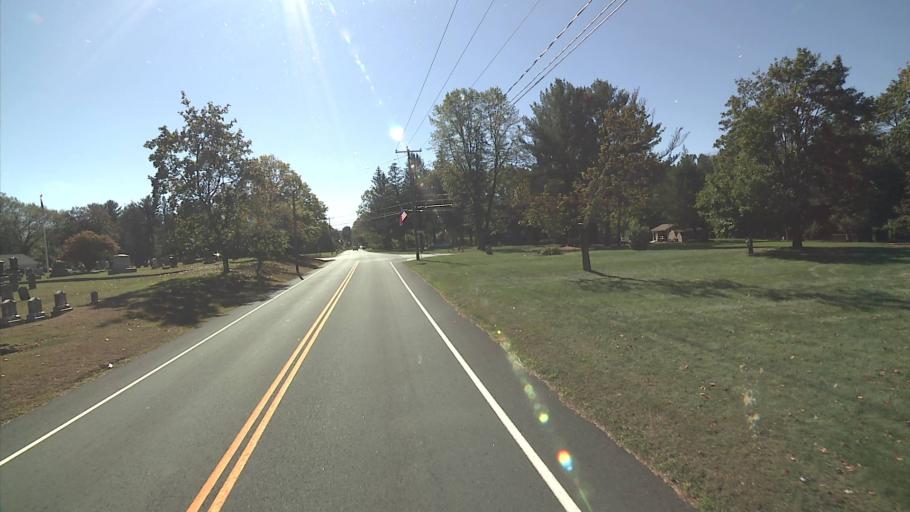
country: US
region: Connecticut
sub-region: Tolland County
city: Somers
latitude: 41.9949
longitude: -72.4507
